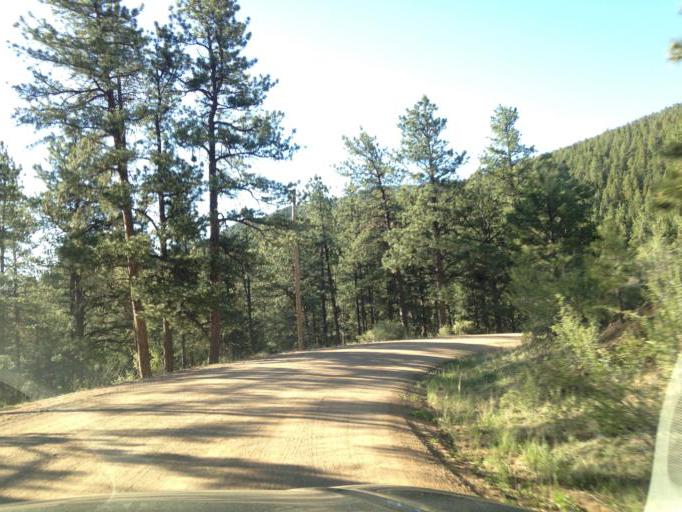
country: US
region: Colorado
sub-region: Jefferson County
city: Evergreen
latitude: 39.4060
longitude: -105.5035
